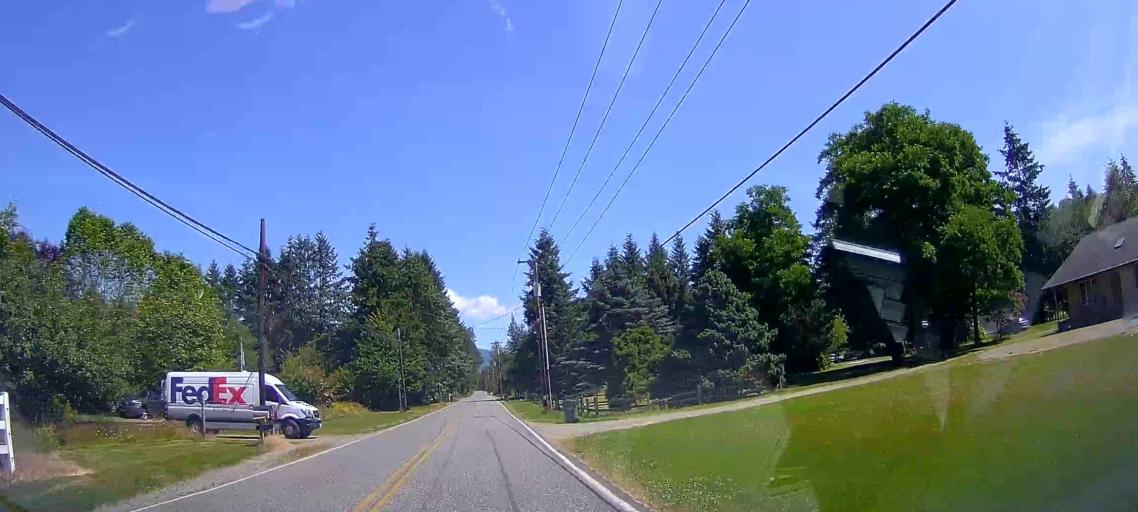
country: US
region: Washington
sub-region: Skagit County
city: Burlington
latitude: 48.5918
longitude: -122.3153
